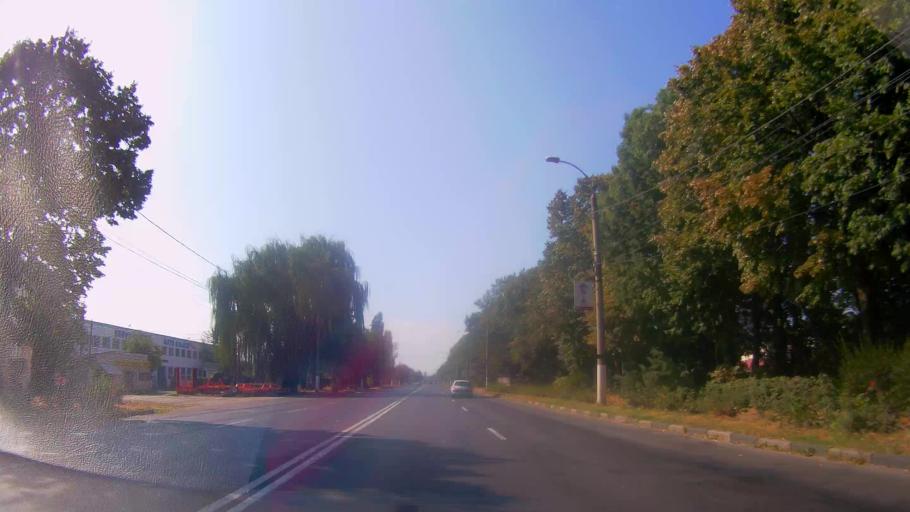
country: RO
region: Giurgiu
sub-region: Comuna Fratesti
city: Remus
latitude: 43.9247
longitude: 25.9743
